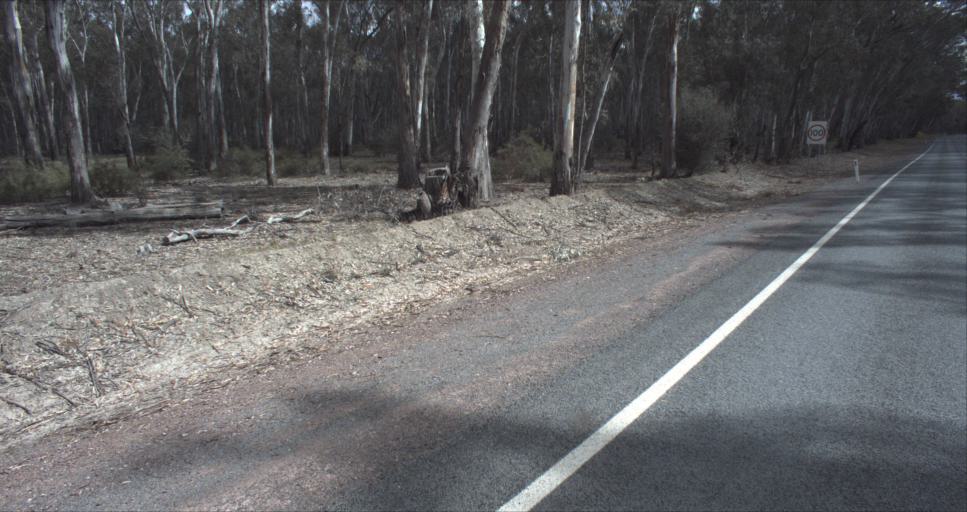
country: AU
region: New South Wales
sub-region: Leeton
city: Leeton
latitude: -34.6399
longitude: 146.3715
